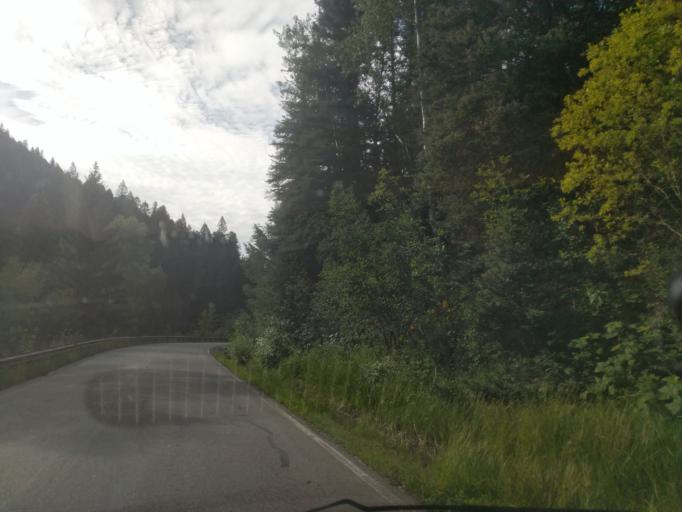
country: US
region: Colorado
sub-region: Garfield County
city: Carbondale
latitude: 39.1074
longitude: -107.2658
